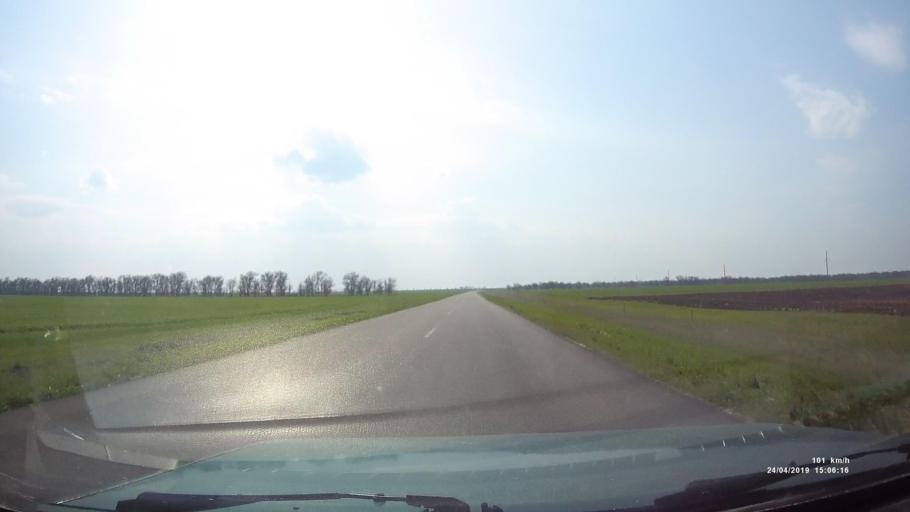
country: RU
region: Rostov
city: Remontnoye
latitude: 46.5590
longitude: 43.4315
